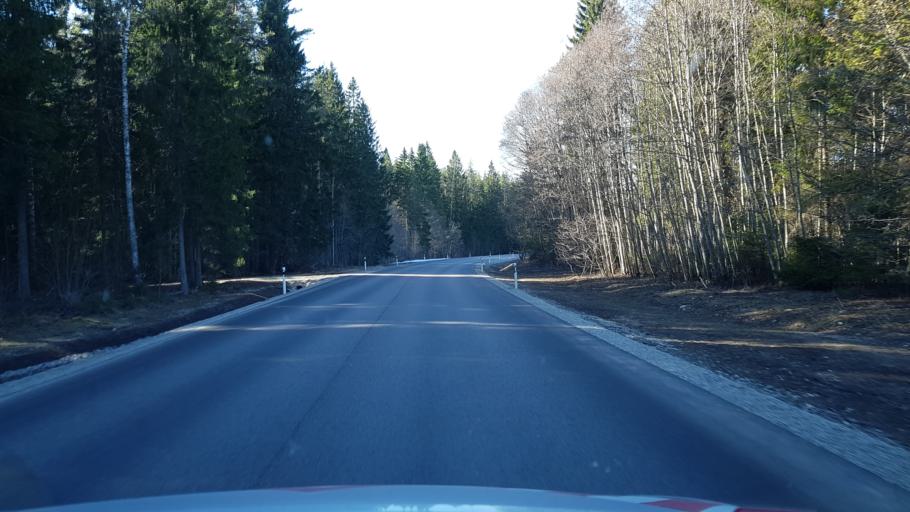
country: EE
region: Laeaene-Virumaa
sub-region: Vinni vald
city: Vinni
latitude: 59.1334
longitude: 26.6016
